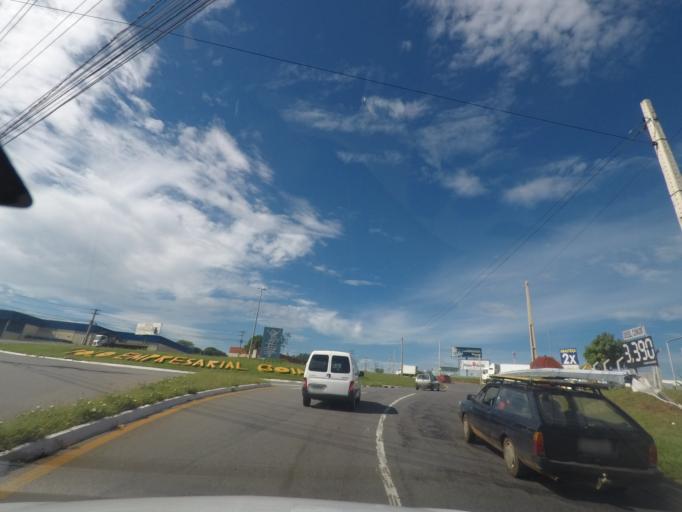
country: BR
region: Goias
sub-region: Aparecida De Goiania
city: Aparecida de Goiania
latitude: -16.7880
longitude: -49.2512
